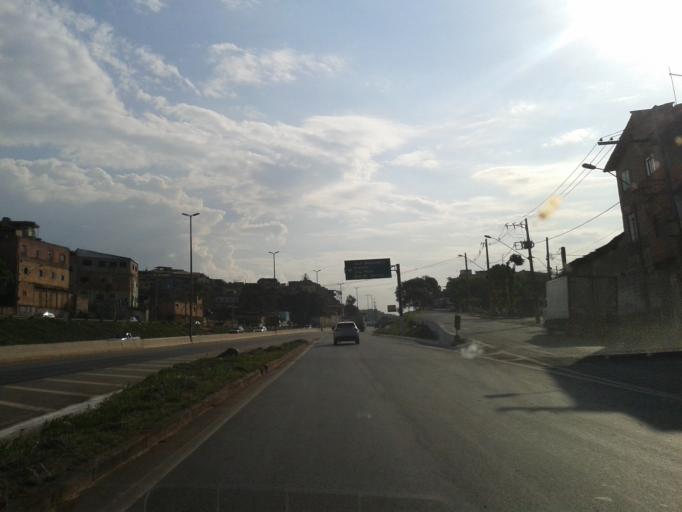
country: BR
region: Minas Gerais
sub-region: Belo Horizonte
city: Belo Horizonte
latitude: -19.8666
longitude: -43.9316
